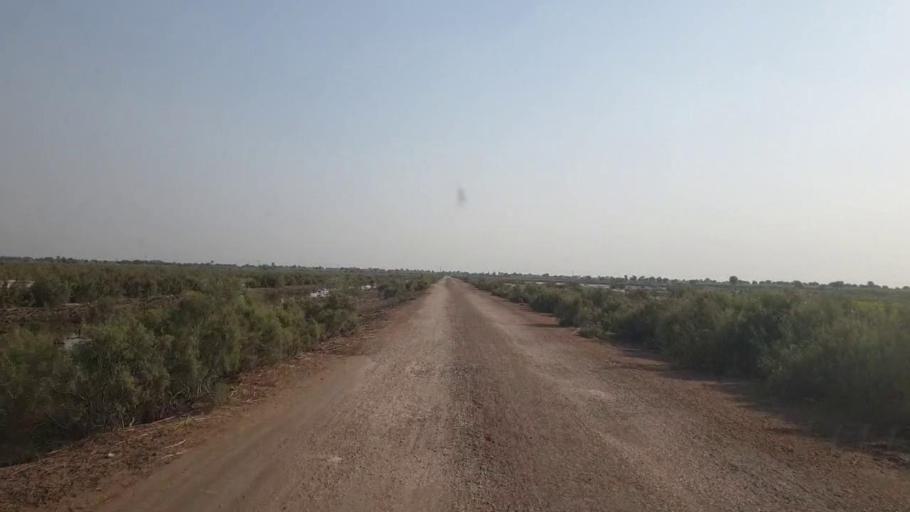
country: PK
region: Sindh
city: Sanghar
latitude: 26.0541
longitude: 68.8968
